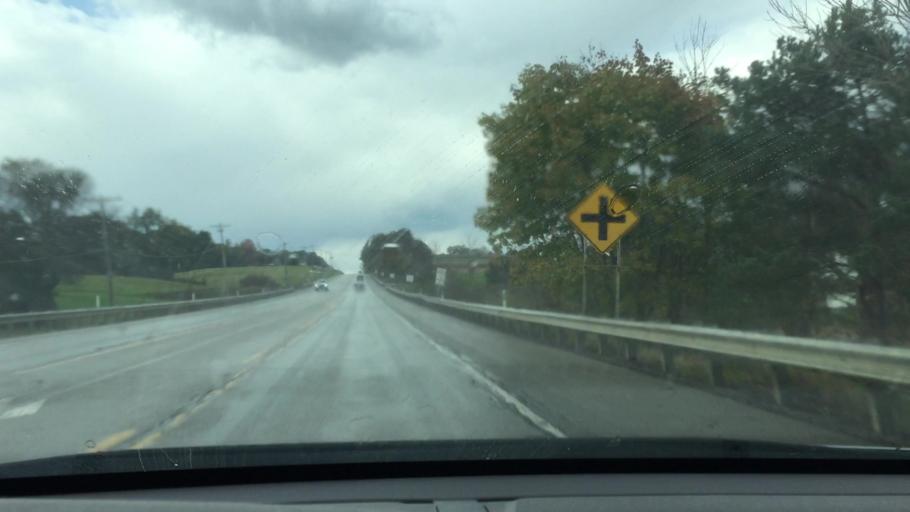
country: US
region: Ohio
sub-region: Mahoning County
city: Lowellville
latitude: 41.0780
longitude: -80.4849
